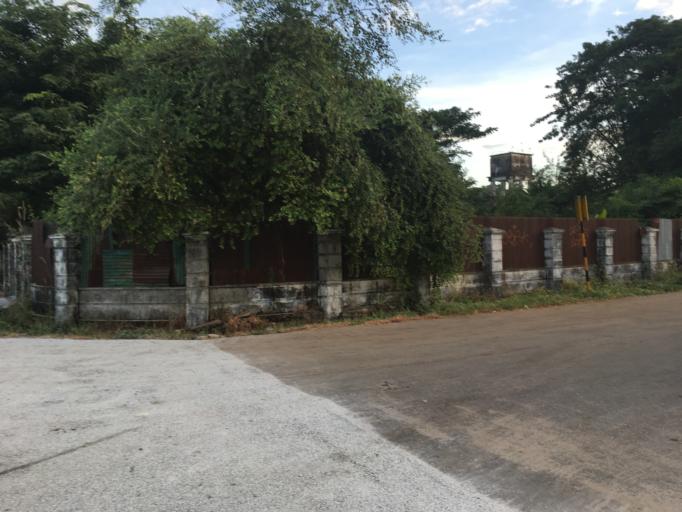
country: MM
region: Mon
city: Mawlamyine
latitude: 16.4643
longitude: 97.6226
